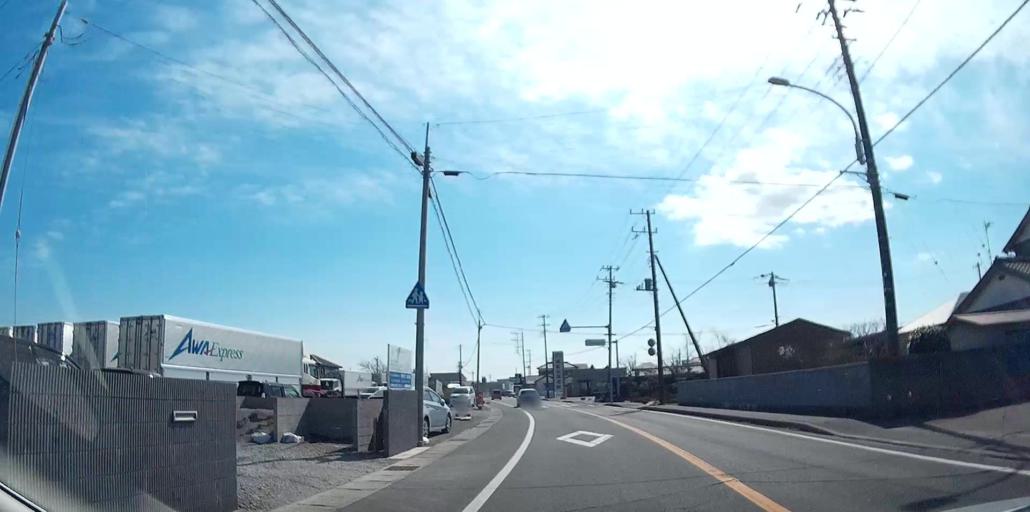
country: JP
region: Chiba
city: Tateyama
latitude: 35.0176
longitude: 139.8577
